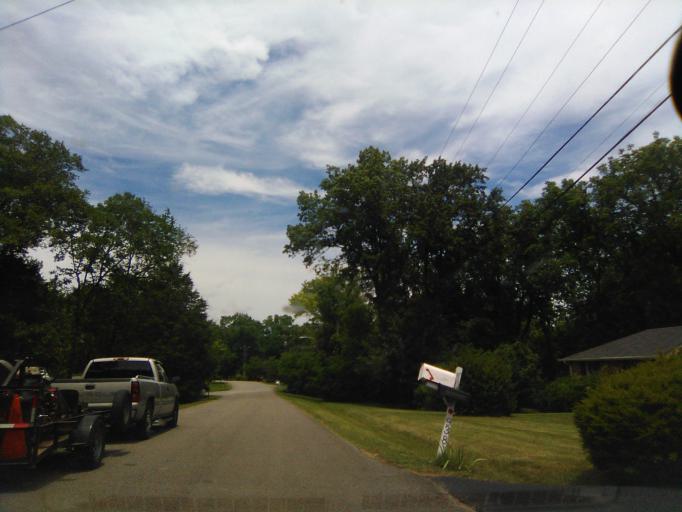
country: US
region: Tennessee
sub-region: Davidson County
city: Belle Meade
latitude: 36.1219
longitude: -86.9037
